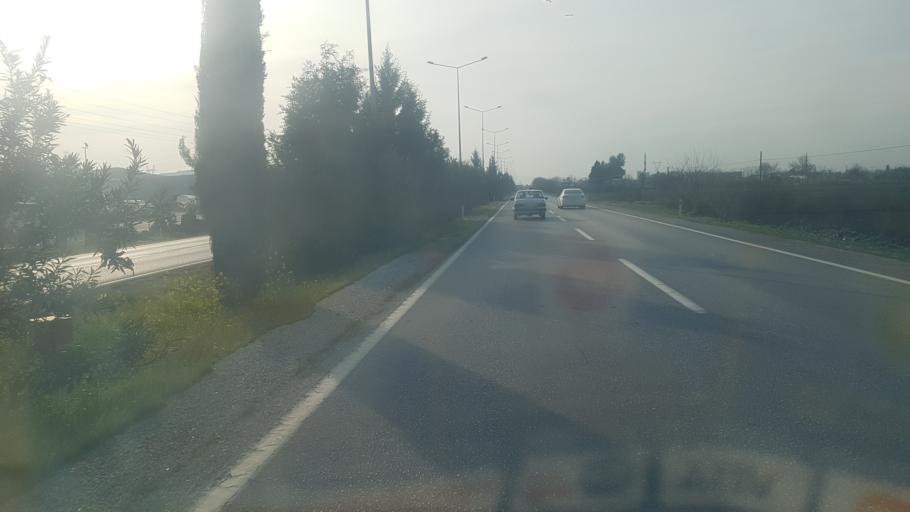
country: TR
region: Osmaniye
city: Toprakkale
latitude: 37.0548
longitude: 36.1343
